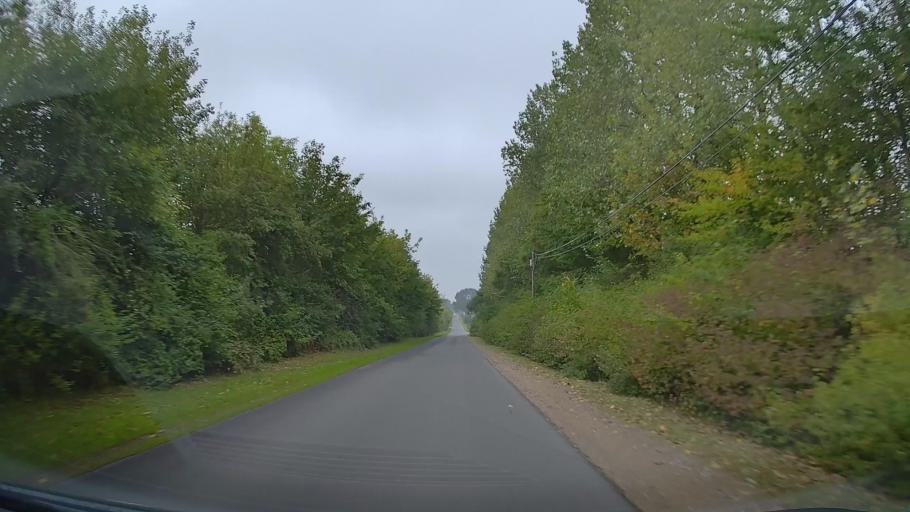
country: DE
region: Mecklenburg-Vorpommern
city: Neubukow
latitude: 54.0488
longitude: 11.6182
